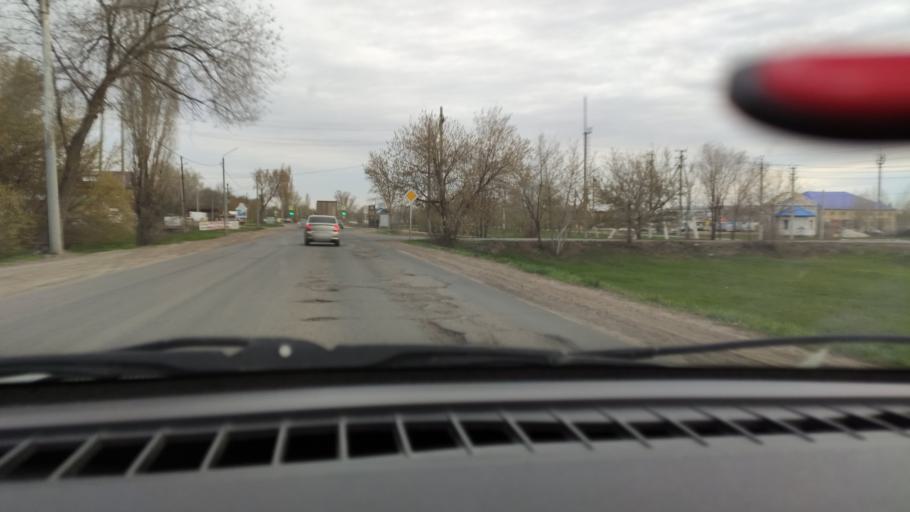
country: RU
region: Orenburg
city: Tatarskaya Kargala
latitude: 51.8671
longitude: 55.1412
